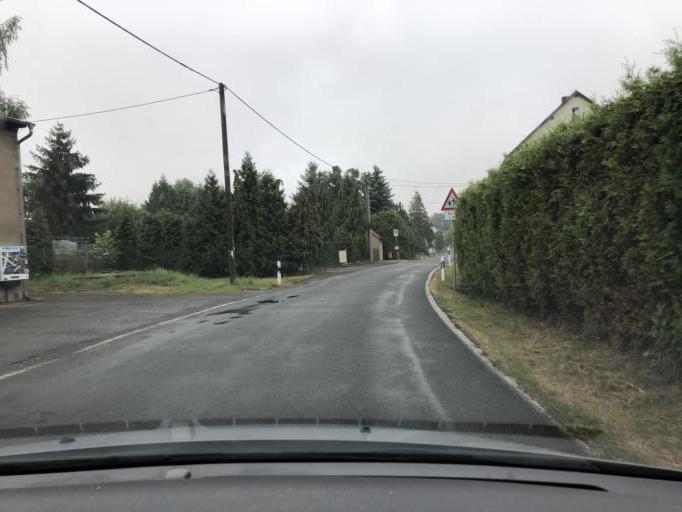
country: DE
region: Saxony
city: Narsdorf
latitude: 50.9984
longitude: 12.6803
